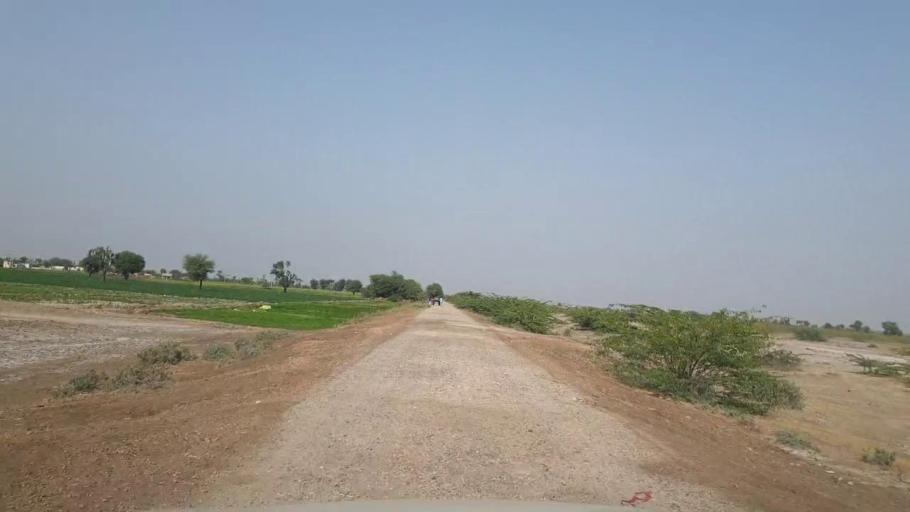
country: PK
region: Sindh
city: Dhoro Naro
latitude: 25.4873
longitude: 69.5815
